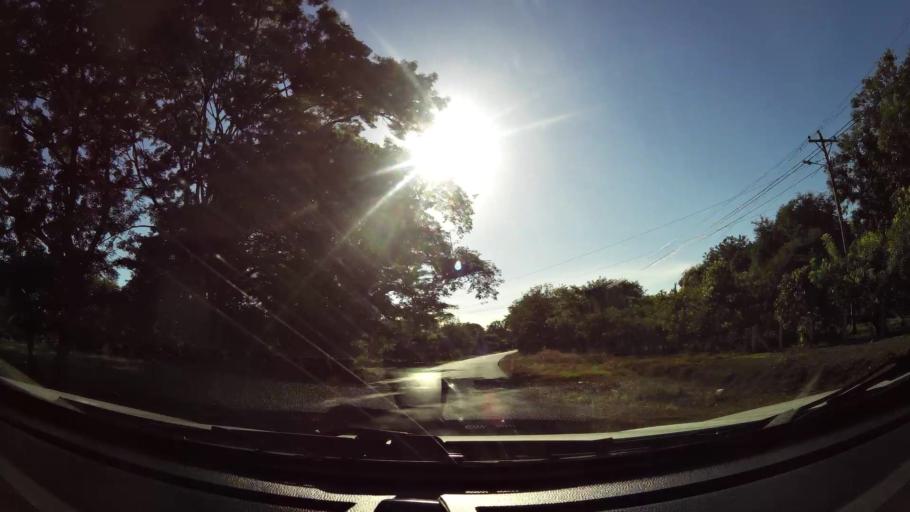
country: CR
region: Guanacaste
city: Sardinal
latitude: 10.4894
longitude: -85.6253
